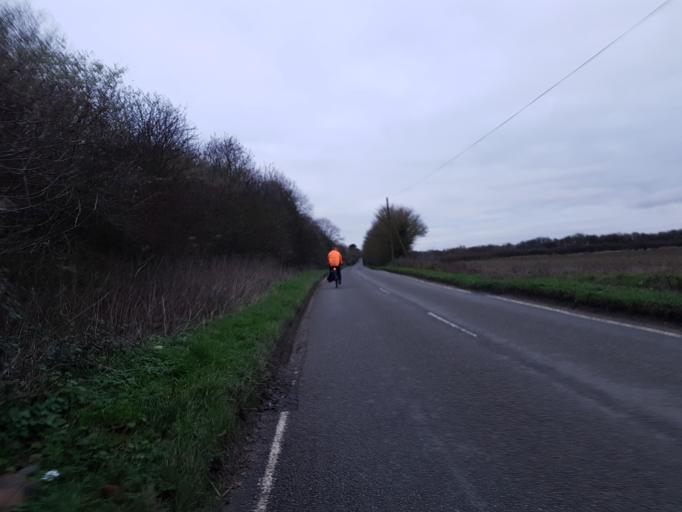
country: GB
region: England
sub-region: Cambridgeshire
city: Fulbourn
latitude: 52.2169
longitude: 0.1867
